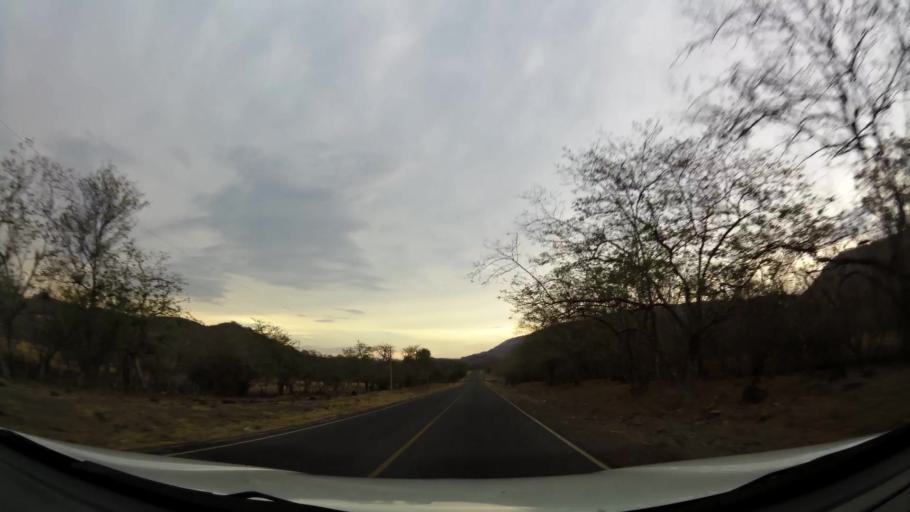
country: NI
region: Leon
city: La Jicaral
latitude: 12.6871
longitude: -86.4165
